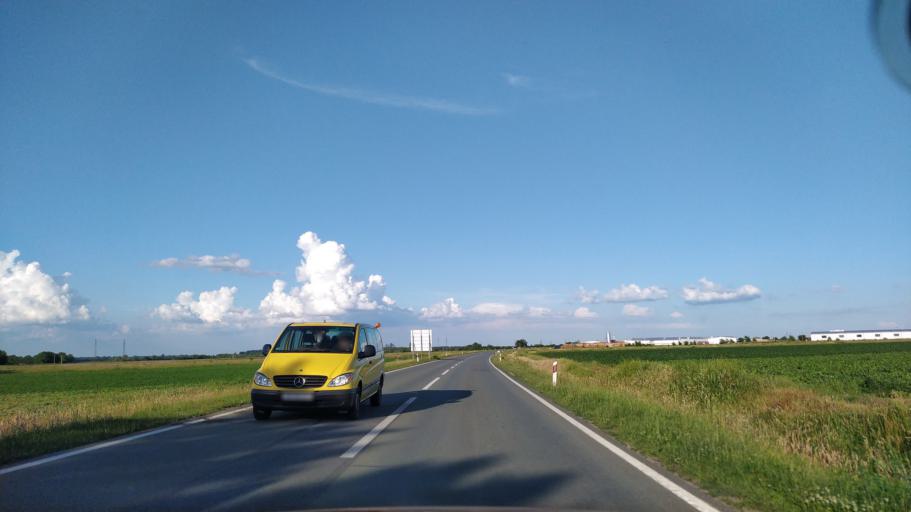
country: HR
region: Virovitick-Podravska
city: Slatina
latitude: 45.7172
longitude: 17.6939
